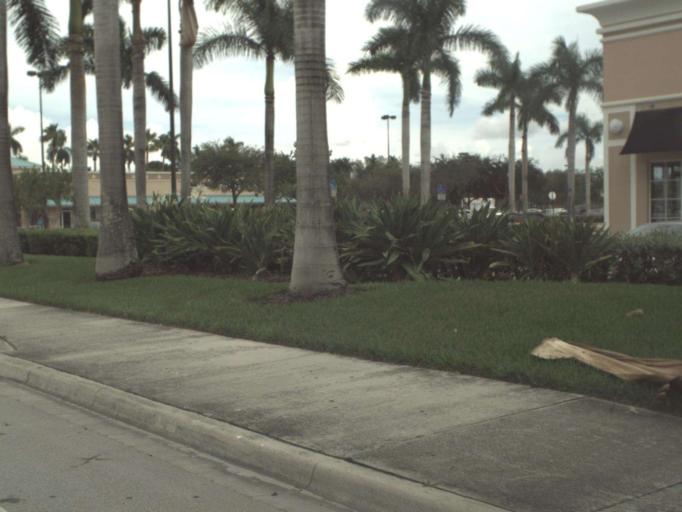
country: US
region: Florida
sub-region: Broward County
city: Hallandale Beach
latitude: 25.9716
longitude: -80.1432
